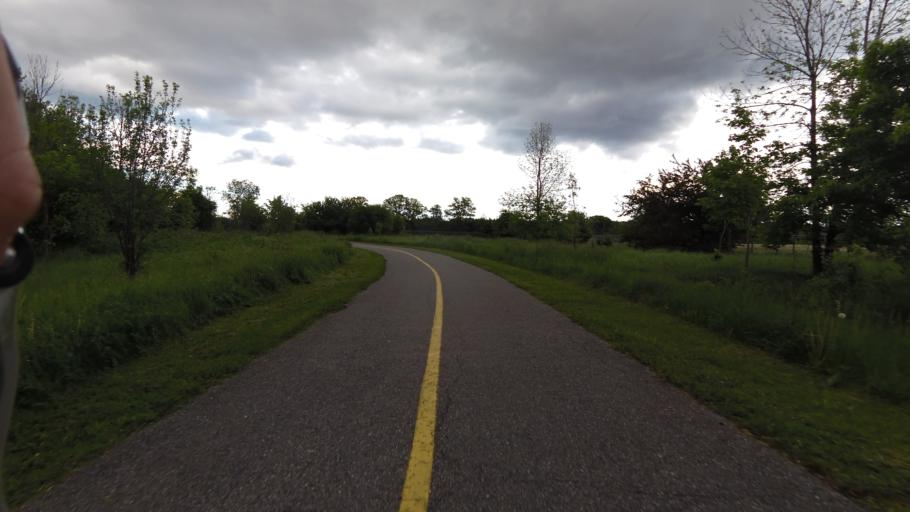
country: CA
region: Ontario
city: Bells Corners
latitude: 45.3331
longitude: -75.8872
